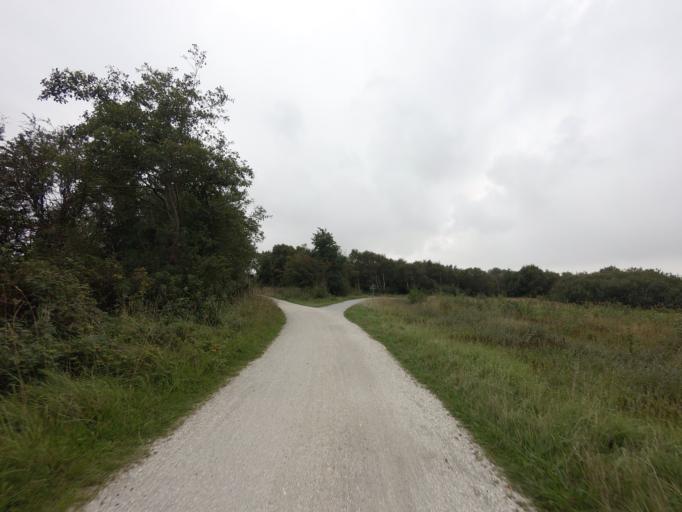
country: NL
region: Friesland
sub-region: Gemeente Schiermonnikoog
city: Schiermonnikoog
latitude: 53.4868
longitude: 6.1598
